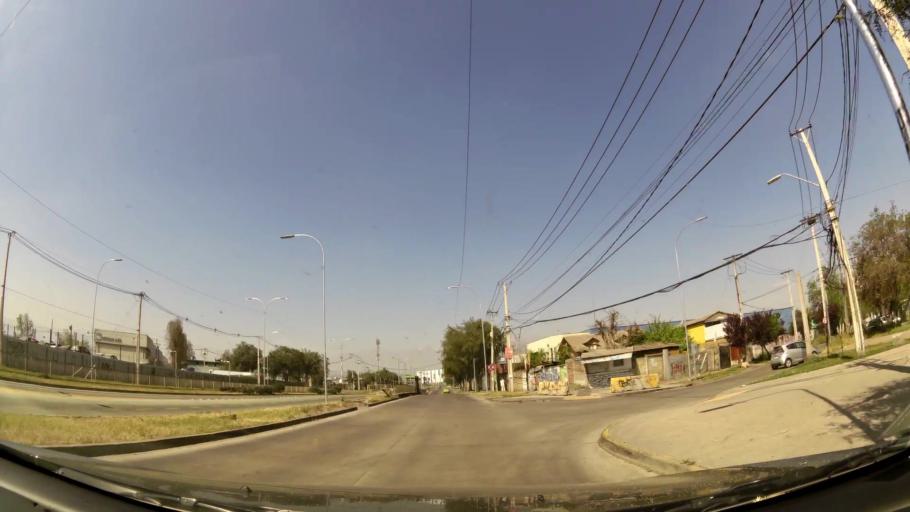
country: CL
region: Santiago Metropolitan
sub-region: Provincia de Santiago
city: Lo Prado
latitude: -33.4025
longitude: -70.6877
